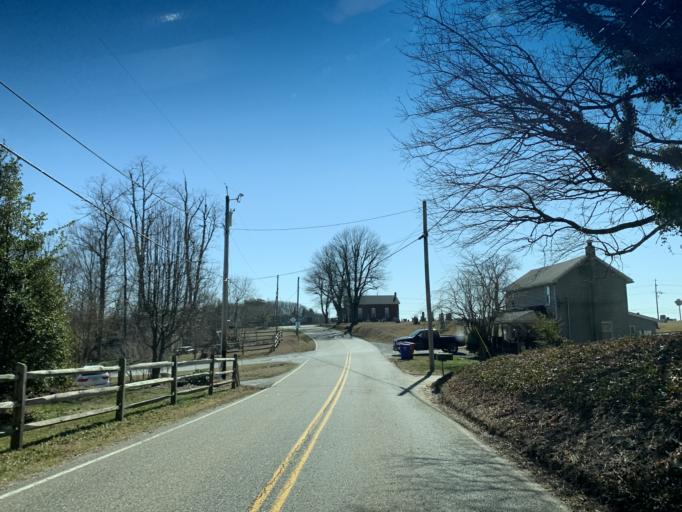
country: US
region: Maryland
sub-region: Cecil County
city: Perryville
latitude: 39.6015
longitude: -76.0701
